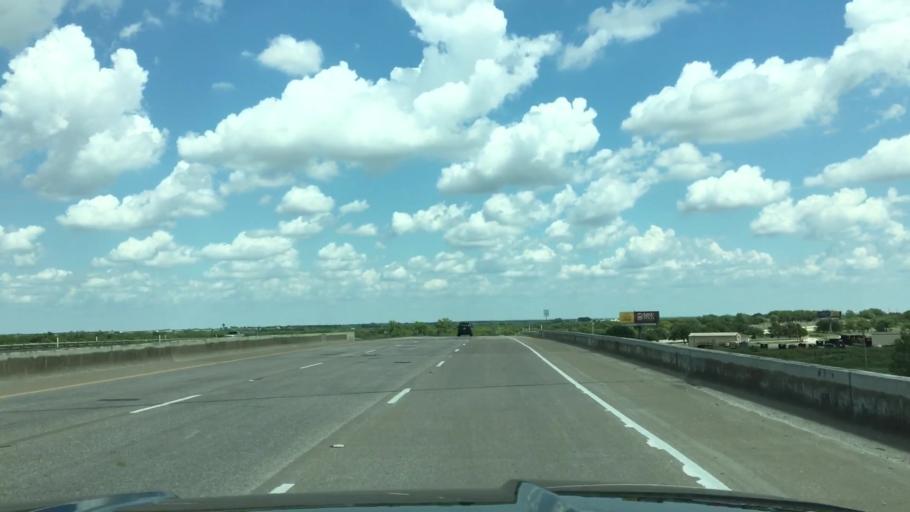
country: US
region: Texas
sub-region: Wise County
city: Rhome
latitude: 33.0454
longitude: -97.4619
